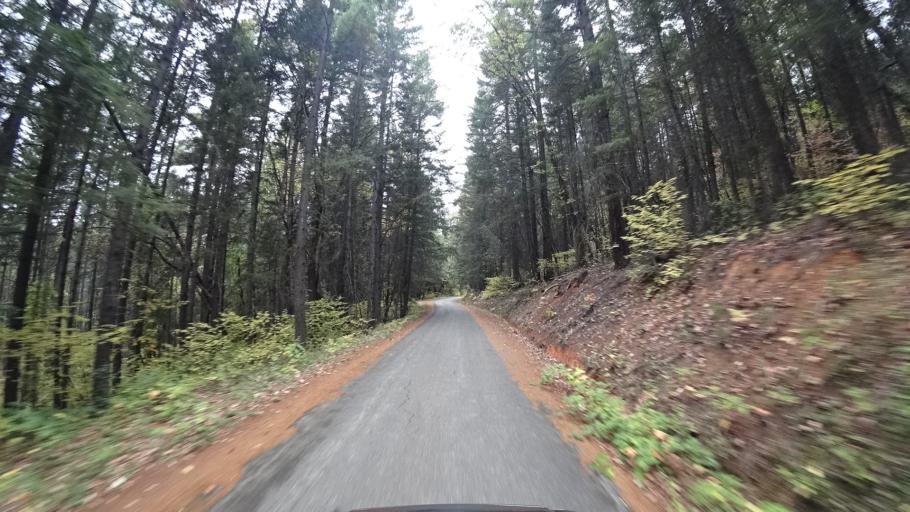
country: US
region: California
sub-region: Siskiyou County
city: Happy Camp
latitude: 41.8062
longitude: -123.3392
